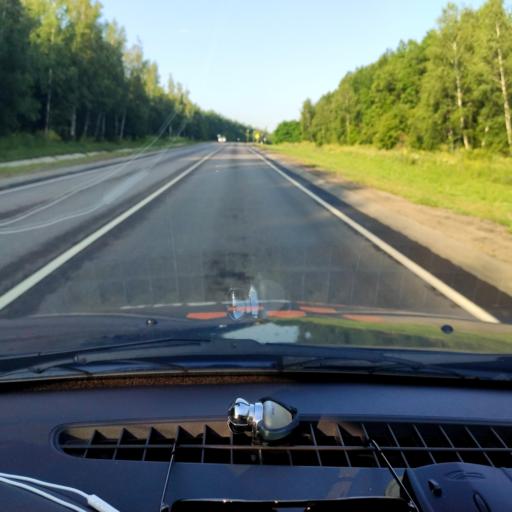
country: RU
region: Lipetsk
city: Izmalkovo
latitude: 52.4562
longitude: 38.0073
